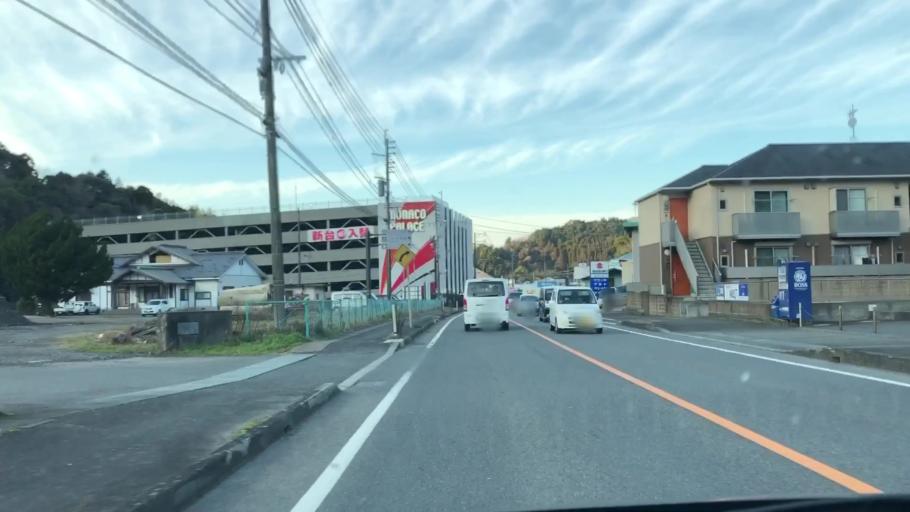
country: JP
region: Kumamoto
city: Minamata
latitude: 32.2218
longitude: 130.4380
